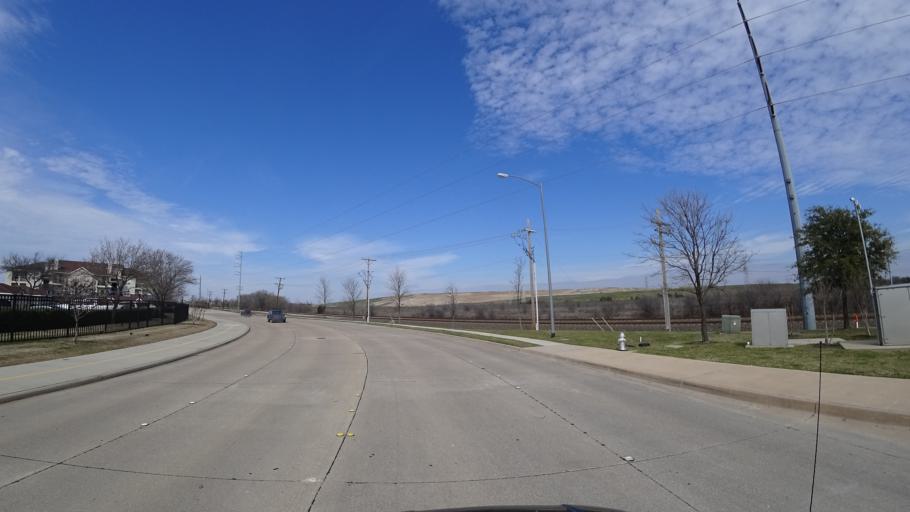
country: US
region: Texas
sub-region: Denton County
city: Lewisville
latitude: 33.0106
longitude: -96.9595
